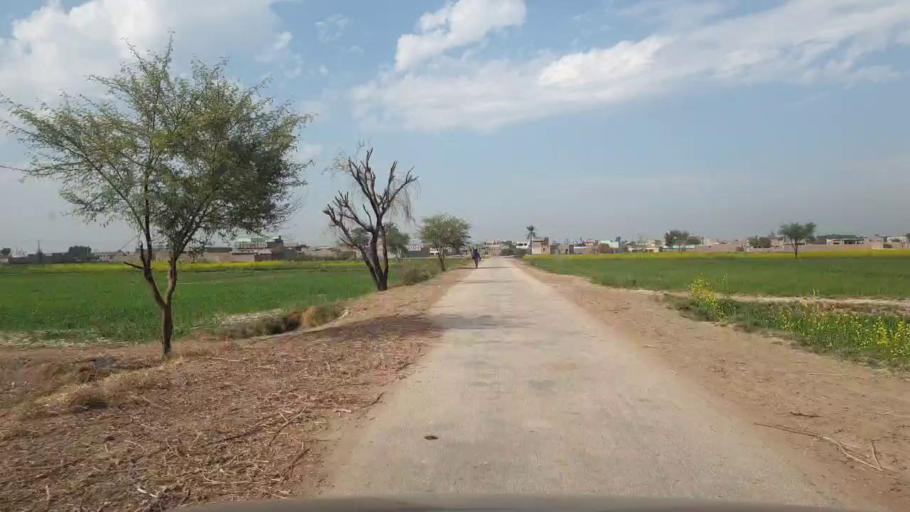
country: PK
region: Sindh
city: Sakrand
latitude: 26.0095
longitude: 68.4113
